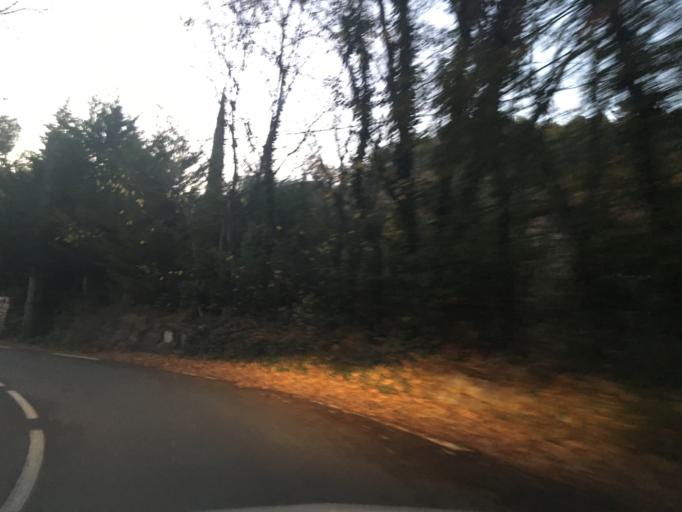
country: FR
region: Provence-Alpes-Cote d'Azur
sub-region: Departement du Var
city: Draguignan
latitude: 43.5359
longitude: 6.4950
